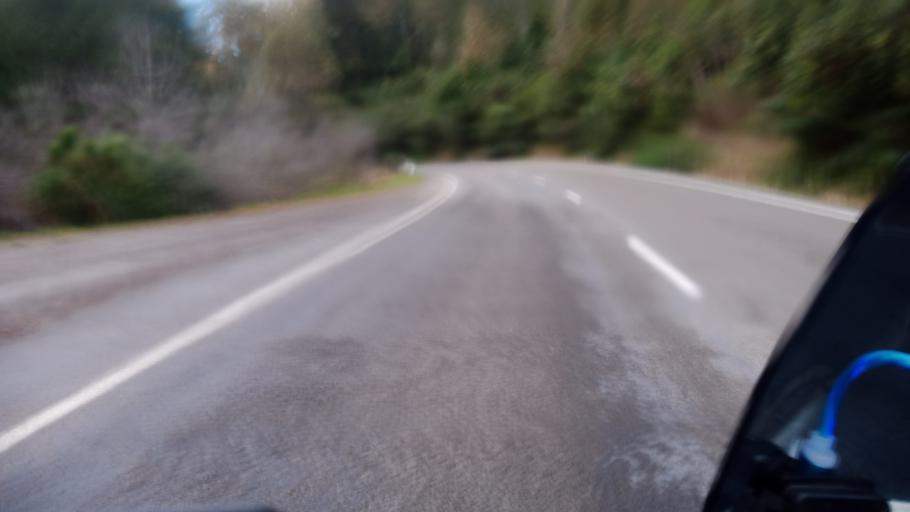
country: NZ
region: Gisborne
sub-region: Gisborne District
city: Gisborne
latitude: -38.0097
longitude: 178.2683
